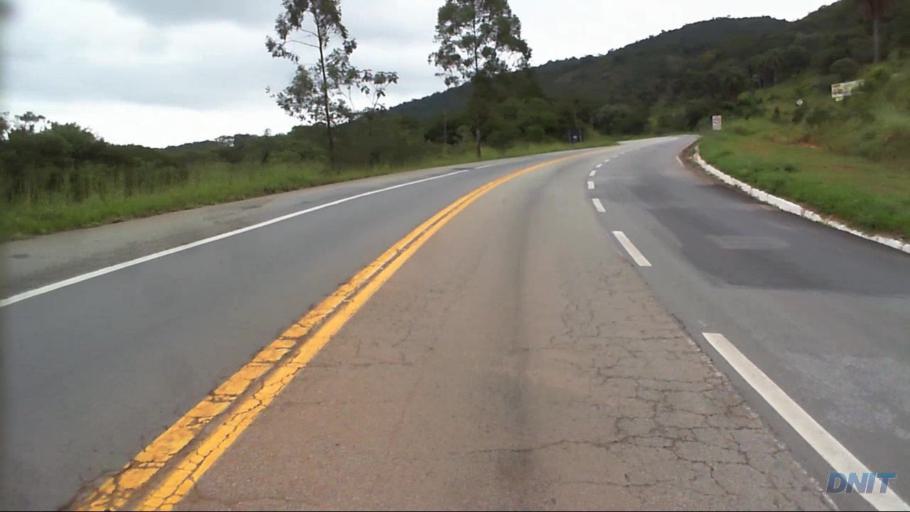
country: BR
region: Minas Gerais
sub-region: Barao De Cocais
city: Barao de Cocais
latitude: -19.7395
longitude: -43.5157
